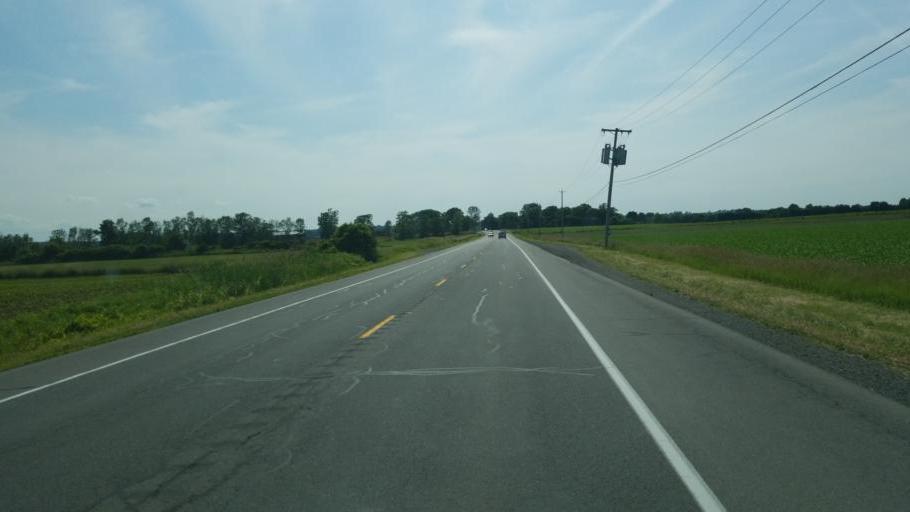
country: US
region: New York
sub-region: Livingston County
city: Lima
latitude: 42.9094
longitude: -77.5757
